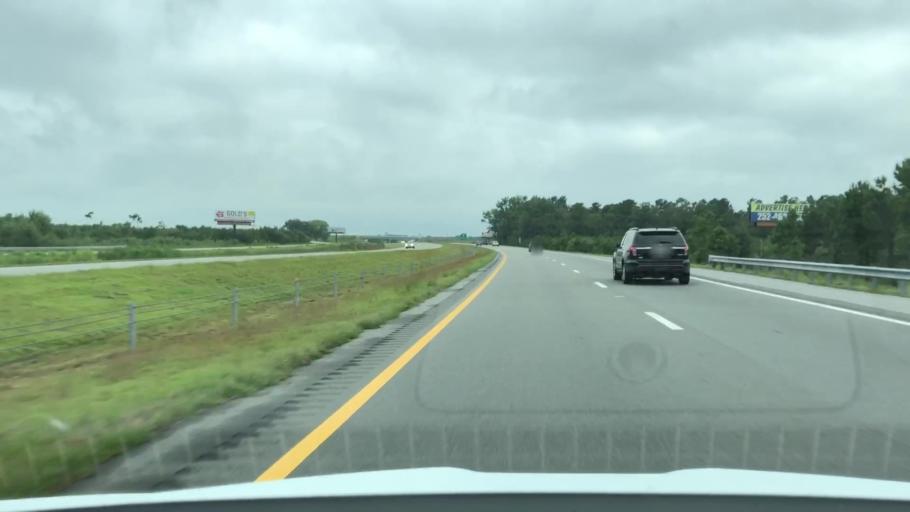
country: US
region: North Carolina
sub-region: Wayne County
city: Elroy
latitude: 35.3995
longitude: -77.8717
